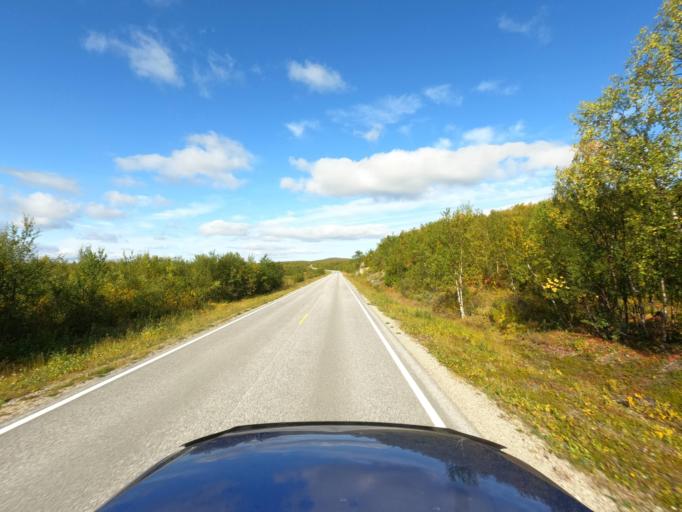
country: NO
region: Finnmark Fylke
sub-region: Karasjok
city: Karasjohka
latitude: 69.5384
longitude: 25.4309
